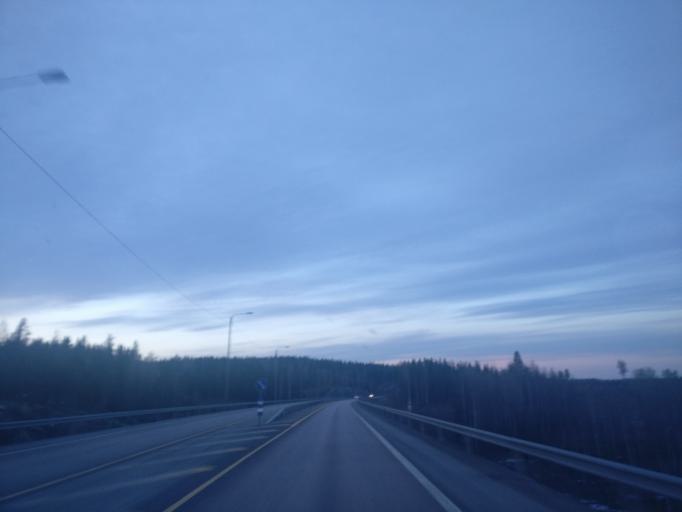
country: FI
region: Central Finland
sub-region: Jyvaeskylae
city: Saeynaetsalo
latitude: 62.2097
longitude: 25.8896
